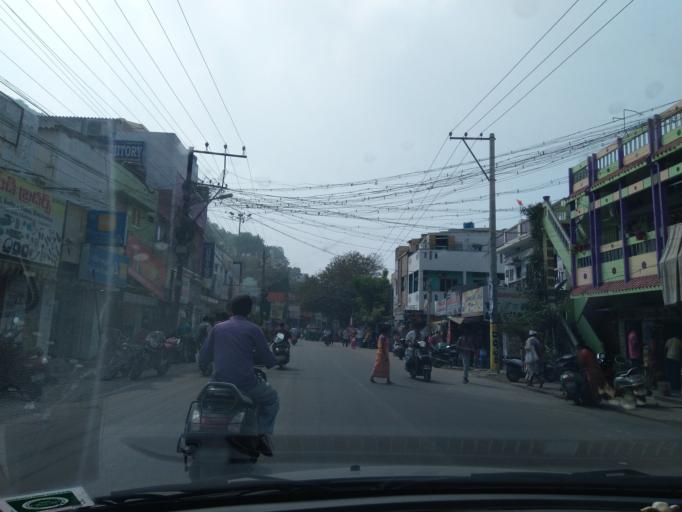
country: IN
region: Andhra Pradesh
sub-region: Krishna
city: Vijayawada
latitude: 16.5313
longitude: 80.6059
